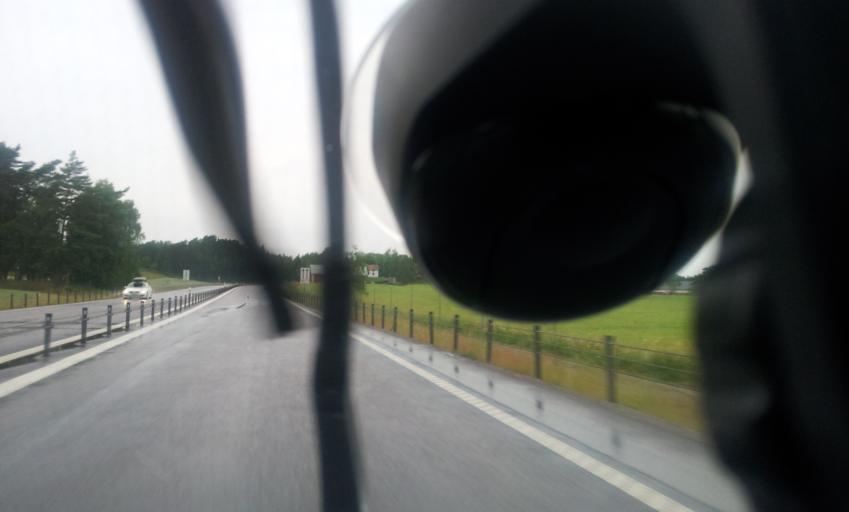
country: SE
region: OEstergoetland
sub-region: Valdemarsviks Kommun
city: Gusum
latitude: 58.3039
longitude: 16.4899
